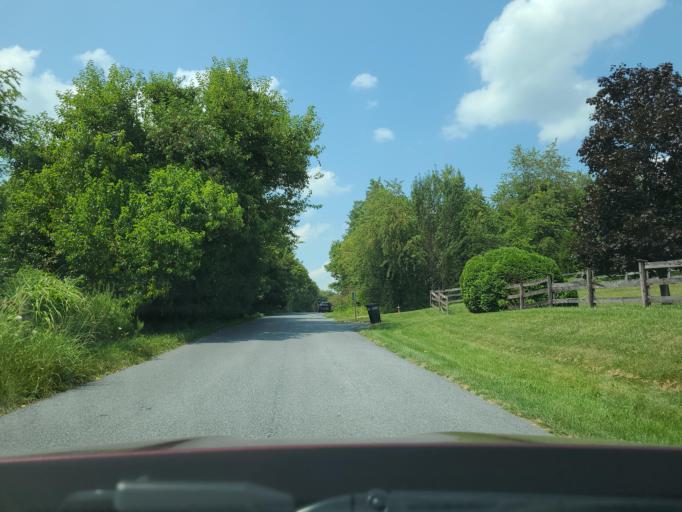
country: US
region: Maryland
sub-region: Frederick County
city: Linganore
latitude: 39.4821
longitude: -77.2461
